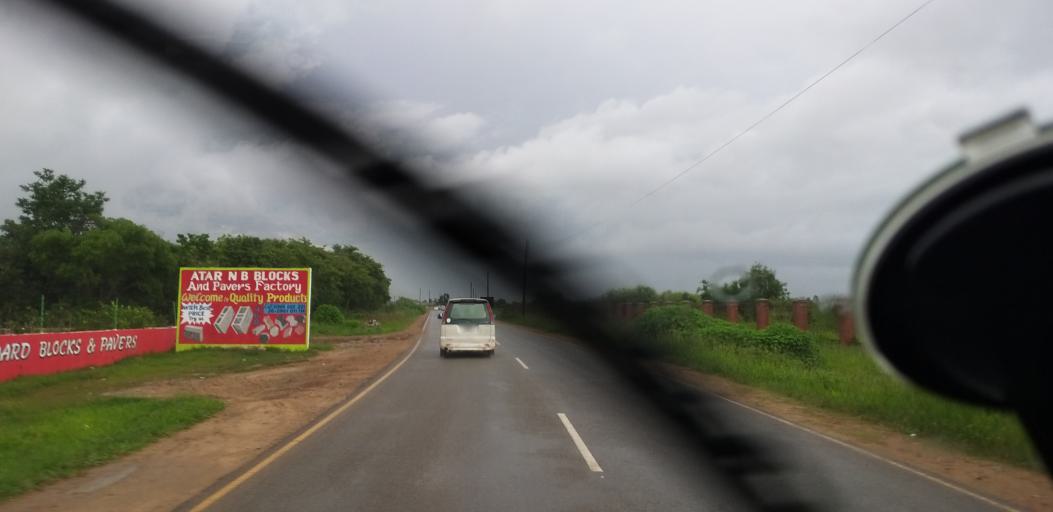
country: ZM
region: Lusaka
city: Lusaka
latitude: -15.4875
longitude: 28.3148
